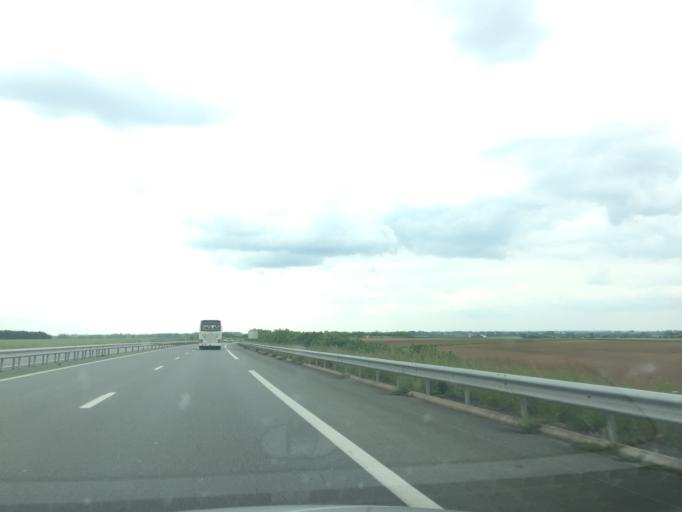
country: FR
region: Pays de la Loire
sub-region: Departement de la Vendee
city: Benet
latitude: 46.3932
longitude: -0.6460
